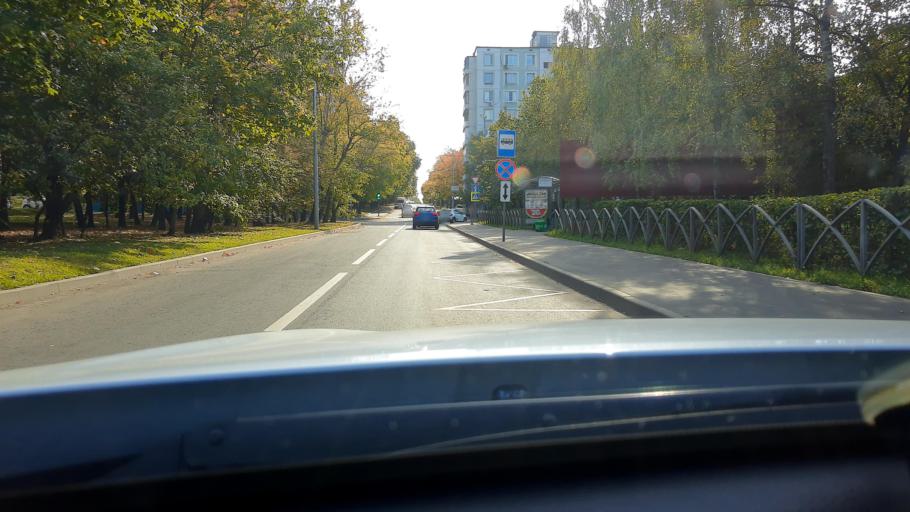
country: RU
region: Moscow
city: Vagonoremont
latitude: 55.8944
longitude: 37.5365
